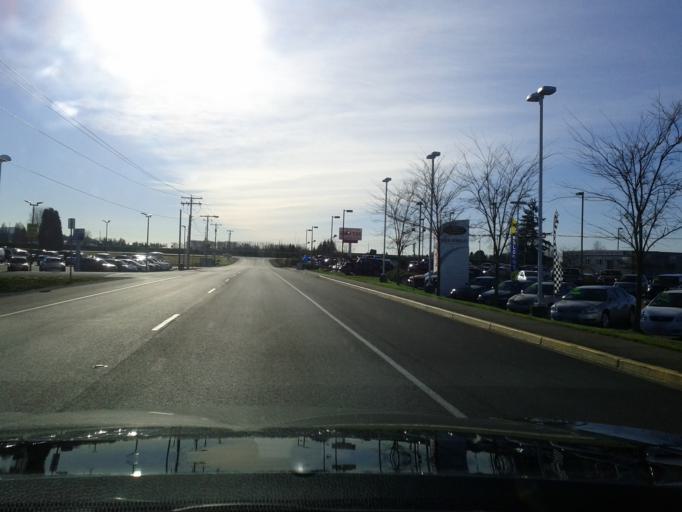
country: US
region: Washington
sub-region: Skagit County
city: Mount Vernon
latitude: 48.4493
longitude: -122.3450
